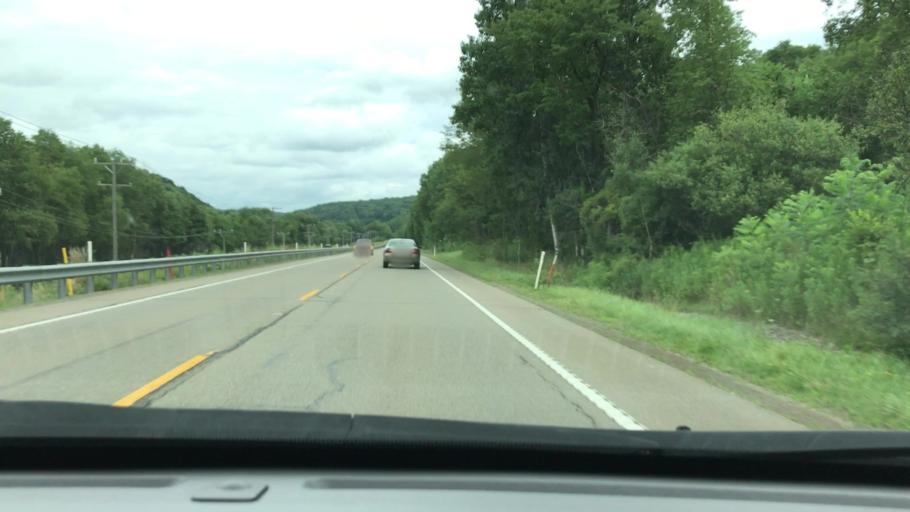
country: US
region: Pennsylvania
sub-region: Elk County
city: Johnsonburg
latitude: 41.5460
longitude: -78.6818
